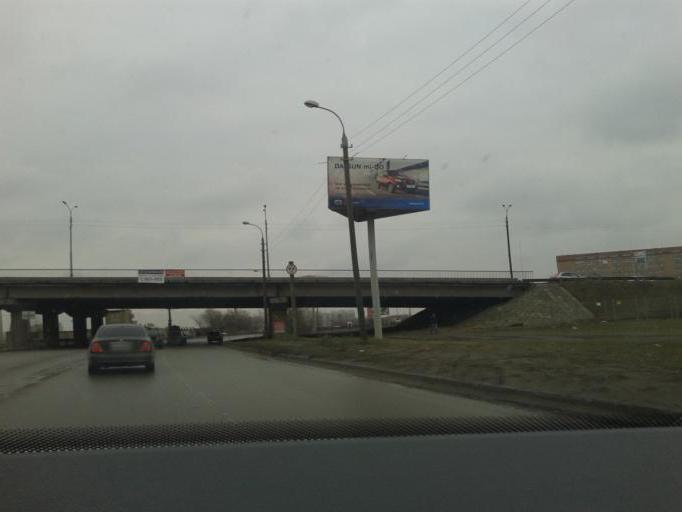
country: RU
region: Volgograd
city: Volgograd
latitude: 48.7657
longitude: 44.5145
